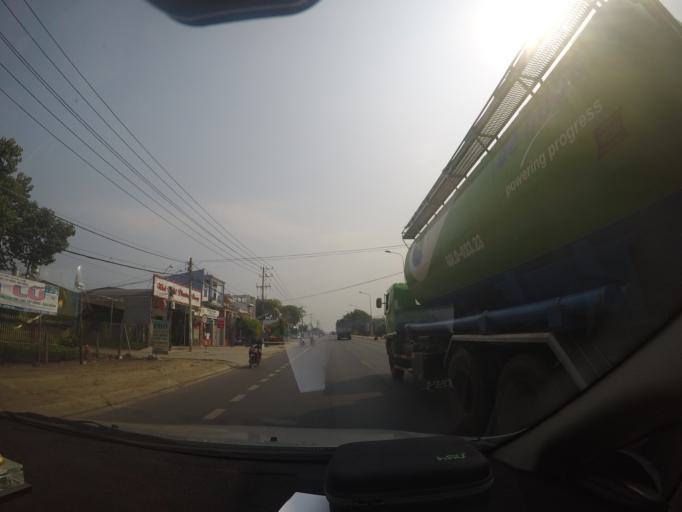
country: VN
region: Dong Nai
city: Tan Phu
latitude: 11.2103
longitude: 107.3653
